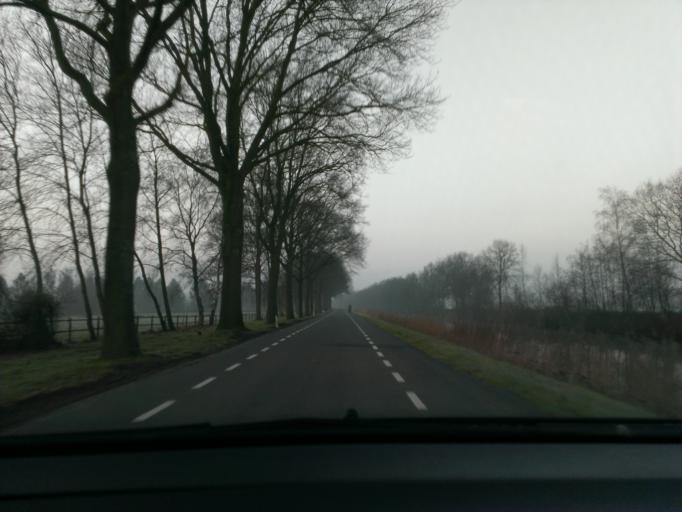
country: NL
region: Gelderland
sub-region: Gemeente Epe
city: Epe
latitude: 52.3292
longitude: 6.0146
